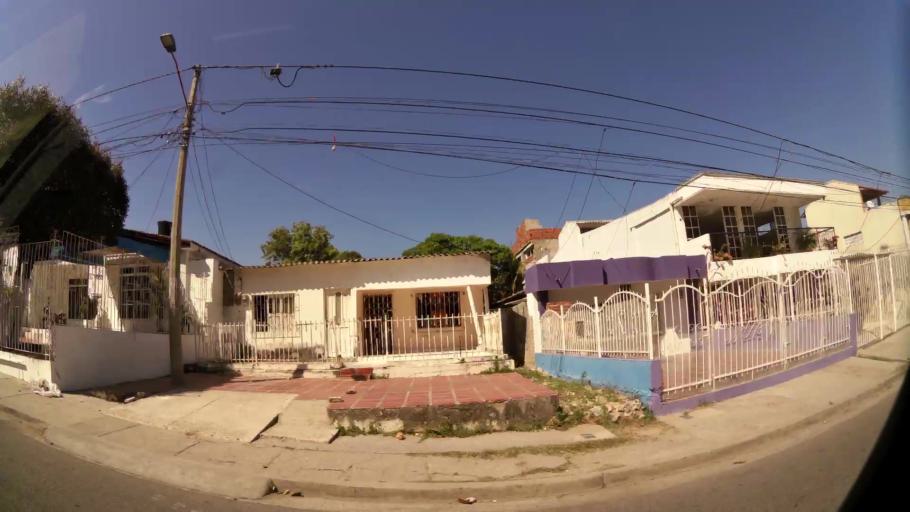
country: CO
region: Bolivar
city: Cartagena
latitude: 10.4393
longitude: -75.5188
